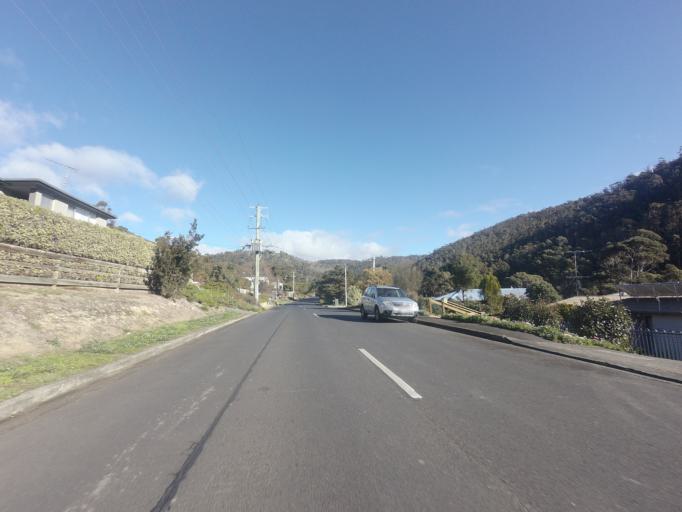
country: AU
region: Tasmania
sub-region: Glenorchy
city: Berriedale
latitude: -42.8169
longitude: 147.2253
